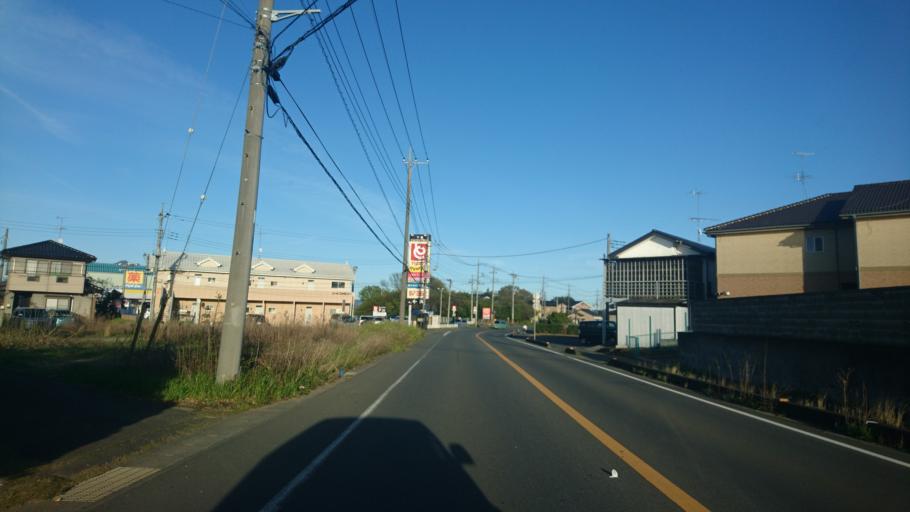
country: JP
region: Ibaraki
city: Ishige
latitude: 36.1929
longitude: 139.9608
